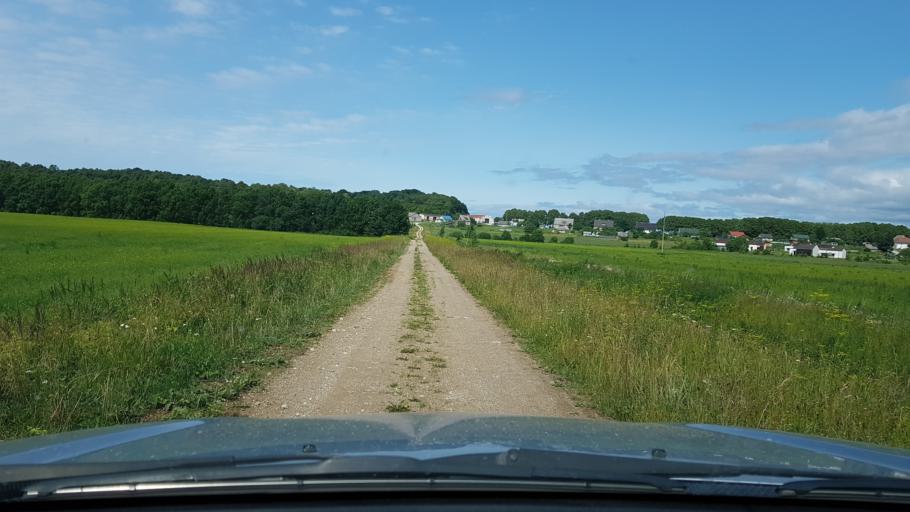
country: EE
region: Ida-Virumaa
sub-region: Sillamaee linn
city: Sillamae
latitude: 59.3675
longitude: 27.8672
